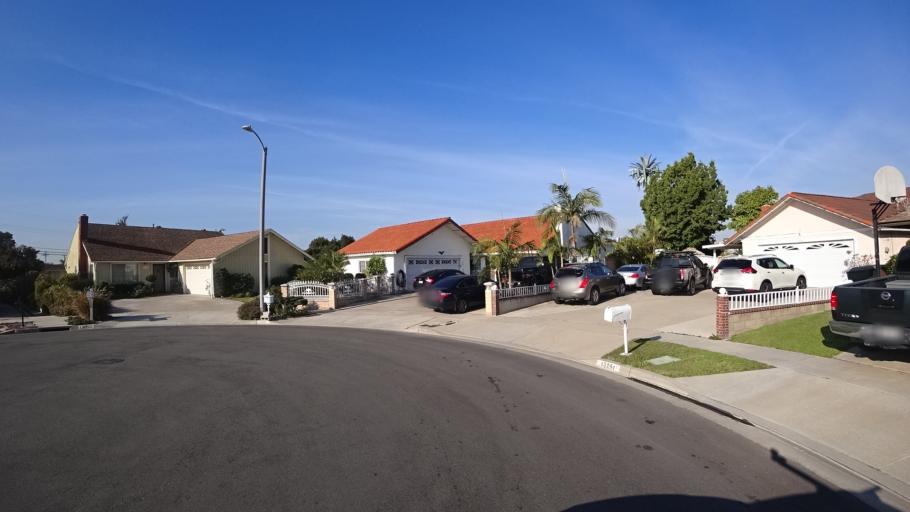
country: US
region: California
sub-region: Orange County
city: Garden Grove
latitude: 33.7731
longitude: -117.9016
